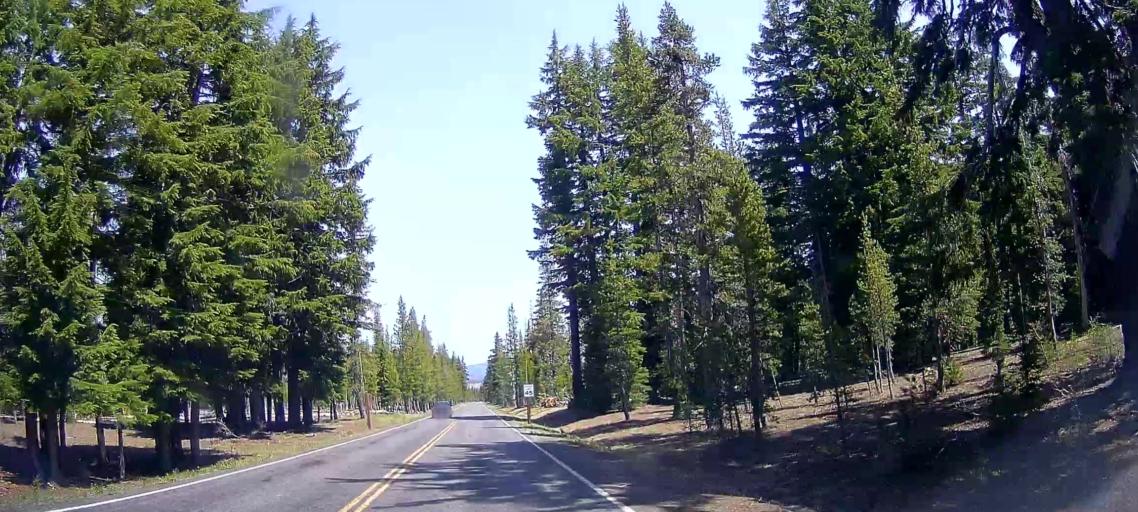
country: US
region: Oregon
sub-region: Jackson County
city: Shady Cove
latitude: 42.9972
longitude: -122.1354
